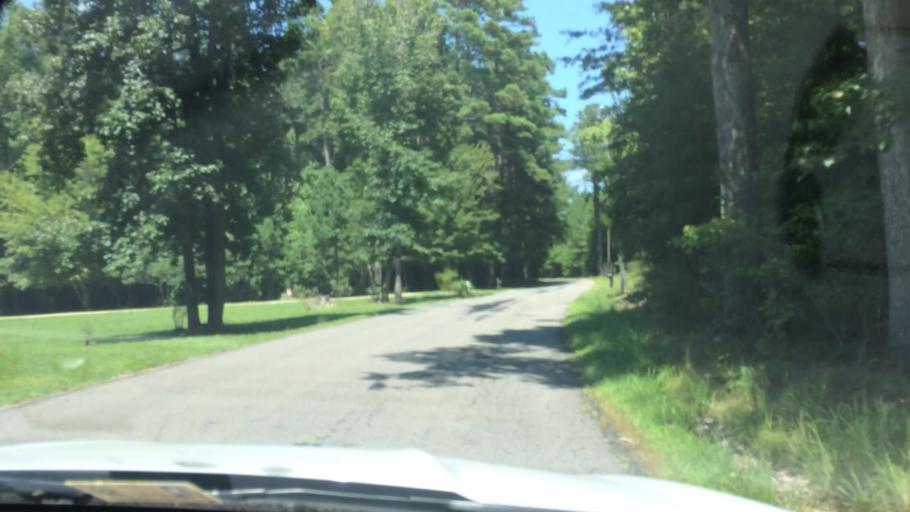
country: US
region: Virginia
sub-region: Charles City County
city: Charles City
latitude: 37.2833
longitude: -76.9321
